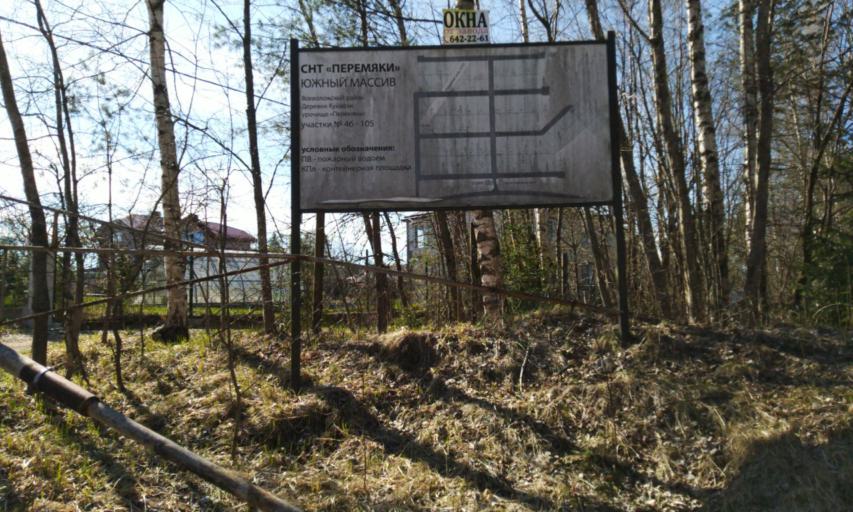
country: RU
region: Leningrad
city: Garbolovo
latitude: 60.3867
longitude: 30.4749
